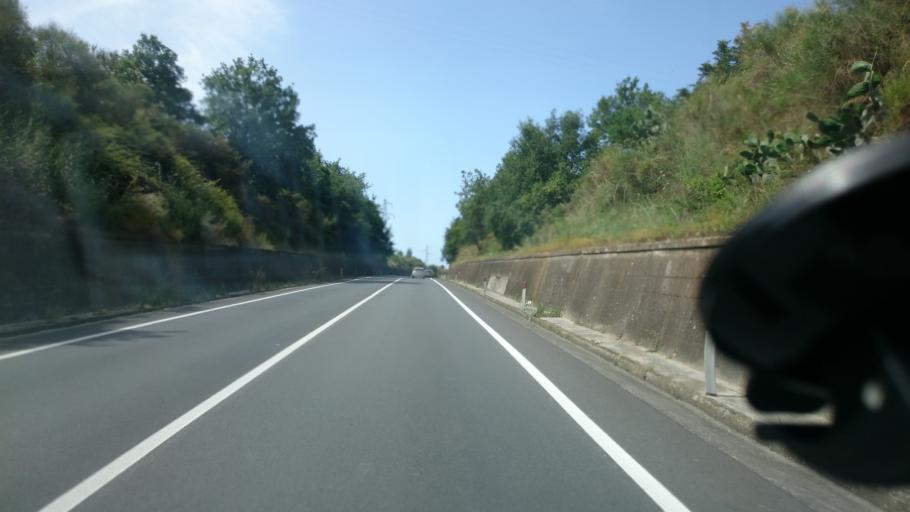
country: IT
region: Calabria
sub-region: Provincia di Cosenza
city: San Nicola Arcella
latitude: 39.8445
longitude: 15.7968
